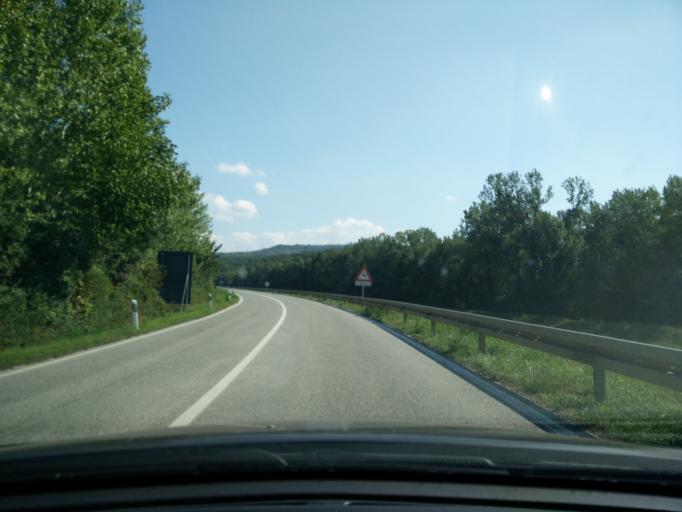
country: HR
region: Istarska
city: Buje
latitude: 45.3570
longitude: 13.7400
